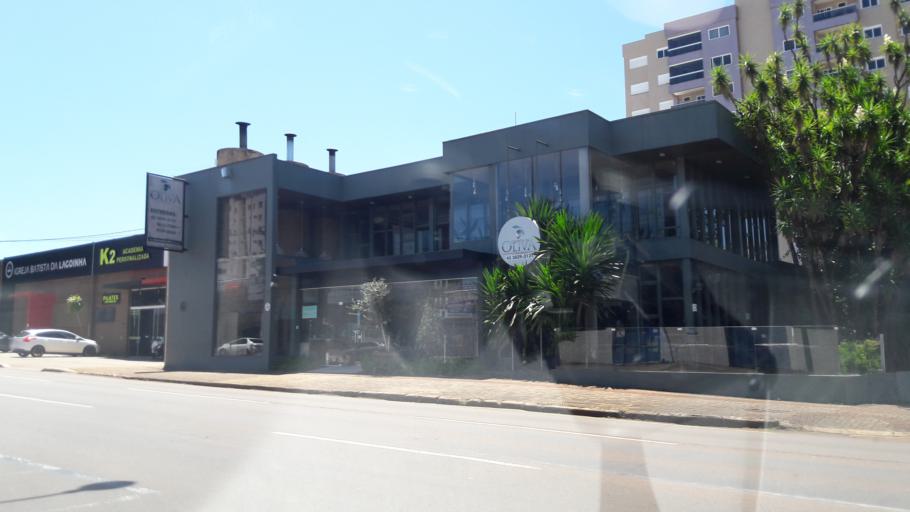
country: BR
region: Parana
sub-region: Cascavel
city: Cascavel
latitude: -24.9513
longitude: -53.4452
